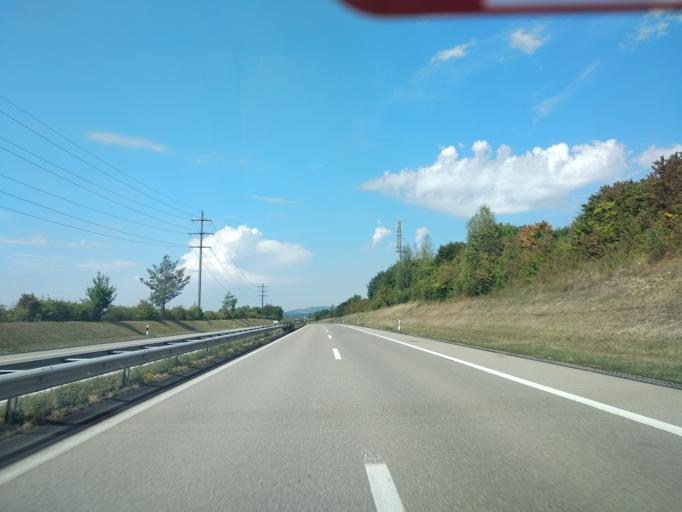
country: CH
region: Thurgau
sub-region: Weinfelden District
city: Maerstetten-Dorf
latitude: 47.6128
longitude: 9.0729
